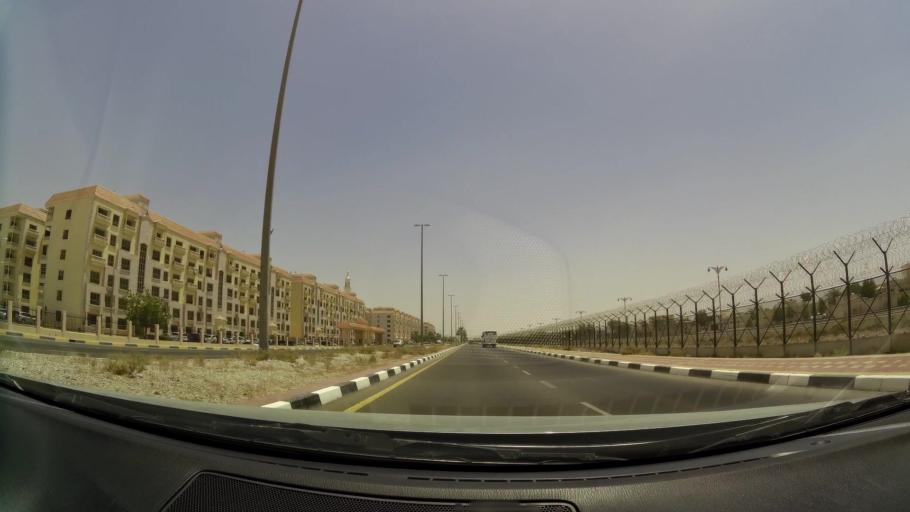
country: OM
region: Al Buraimi
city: Al Buraymi
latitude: 24.2684
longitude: 55.7766
